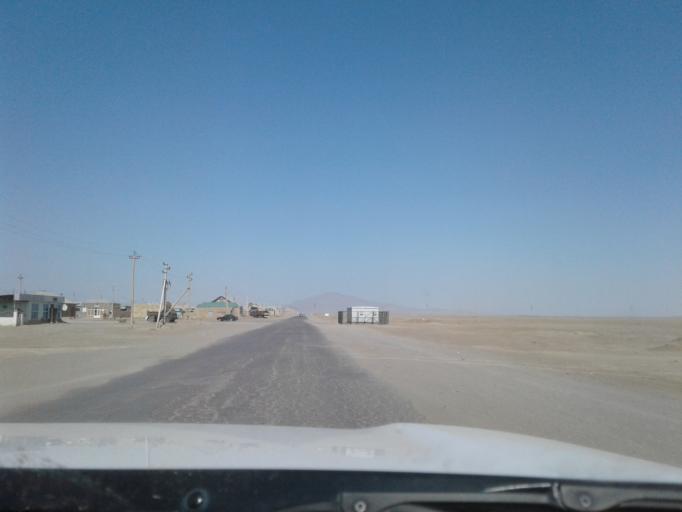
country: TM
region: Balkan
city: Gumdag
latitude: 39.1968
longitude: 54.5983
